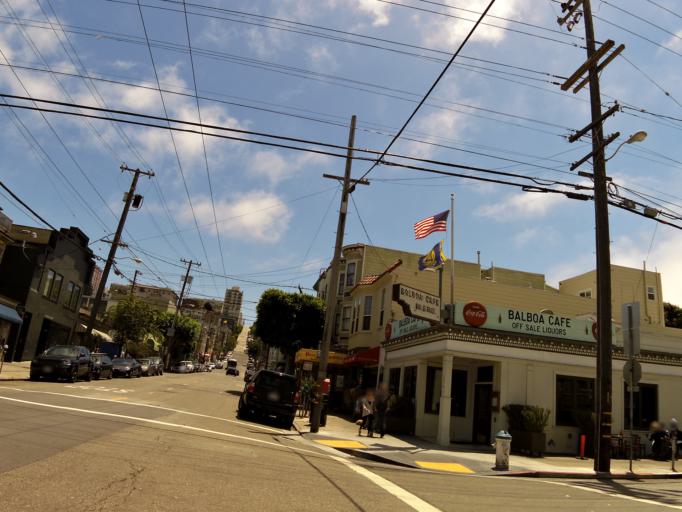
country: US
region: California
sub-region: San Francisco County
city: San Francisco
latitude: 37.7990
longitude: -122.4359
